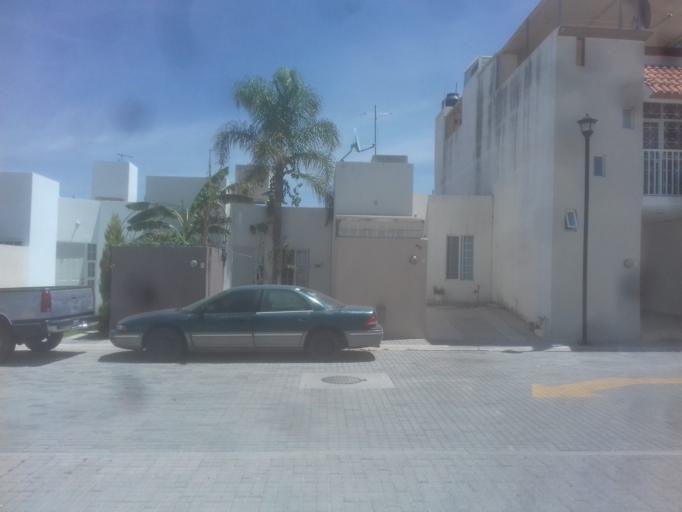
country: MX
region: Aguascalientes
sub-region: Aguascalientes
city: San Sebastian [Fraccionamiento]
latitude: 21.8109
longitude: -102.3001
